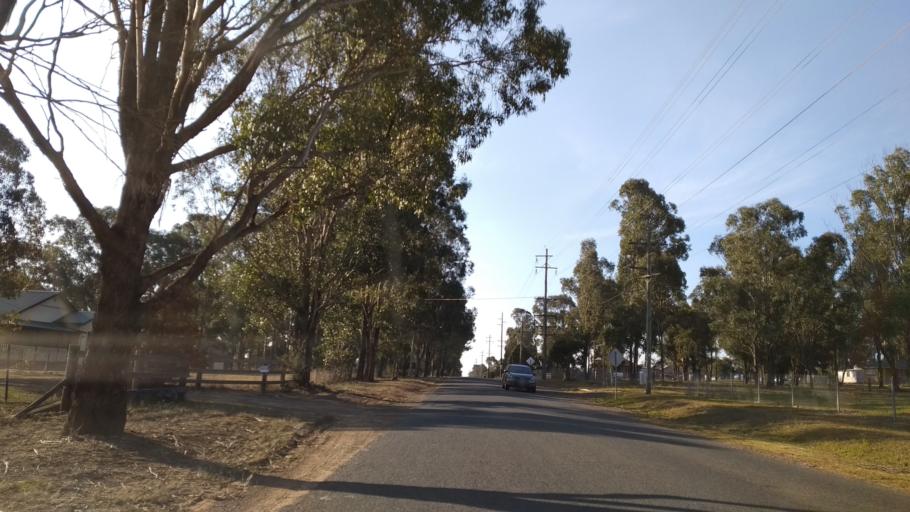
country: AU
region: New South Wales
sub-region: Penrith Municipality
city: Werrington Downs
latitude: -33.7053
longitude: 150.7327
